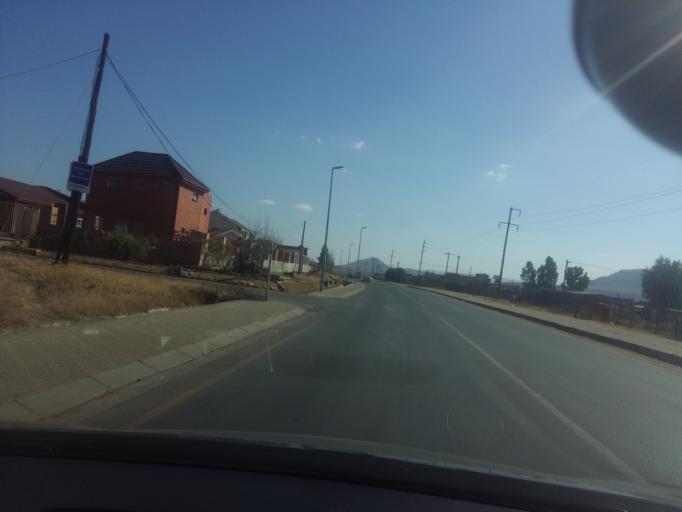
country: LS
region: Maseru
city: Maseru
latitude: -29.3409
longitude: 27.4501
